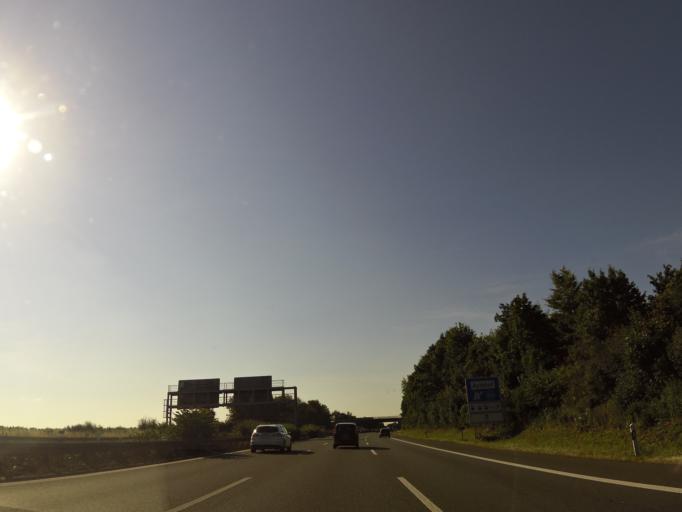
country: DE
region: Bavaria
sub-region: Regierungsbezirk Mittelfranken
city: Erlangen
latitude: 49.5546
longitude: 11.0067
